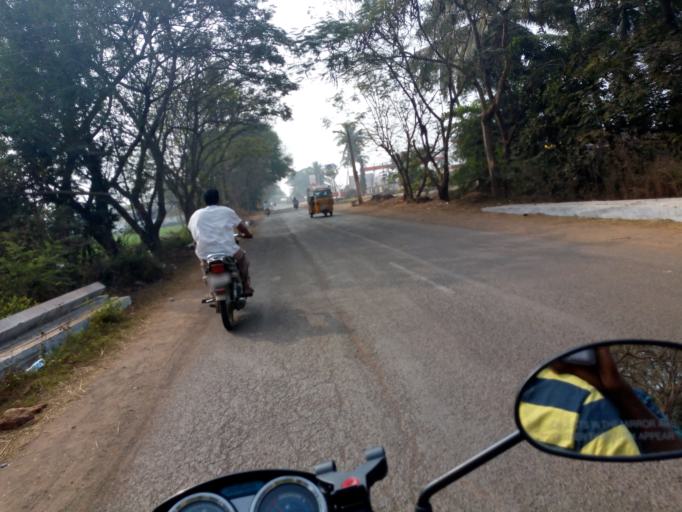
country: IN
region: Andhra Pradesh
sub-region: West Godavari
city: Tadepallegudem
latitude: 16.8117
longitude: 81.4083
